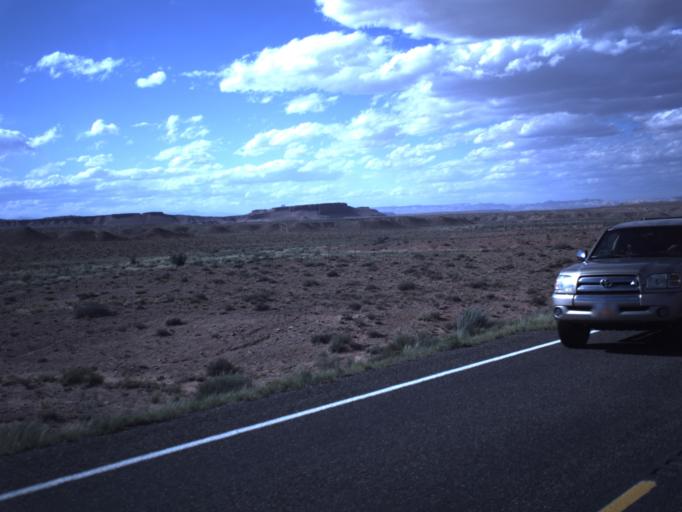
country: US
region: Utah
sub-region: Emery County
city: Ferron
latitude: 38.3049
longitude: -110.6703
